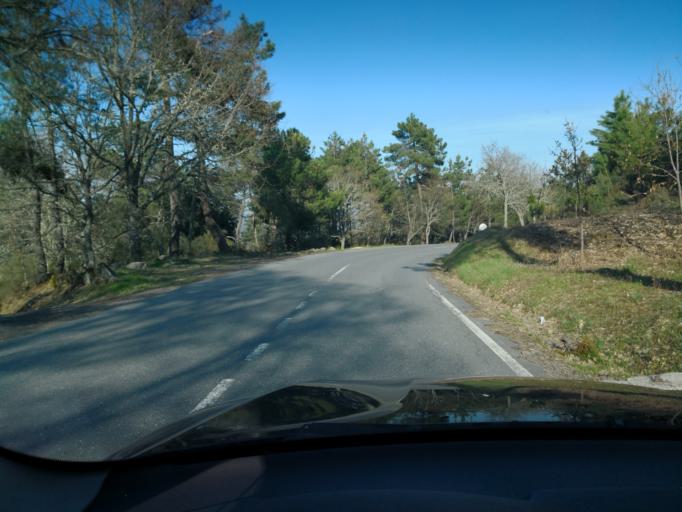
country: PT
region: Vila Real
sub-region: Sabrosa
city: Sabrosa
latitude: 41.3577
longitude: -7.6305
